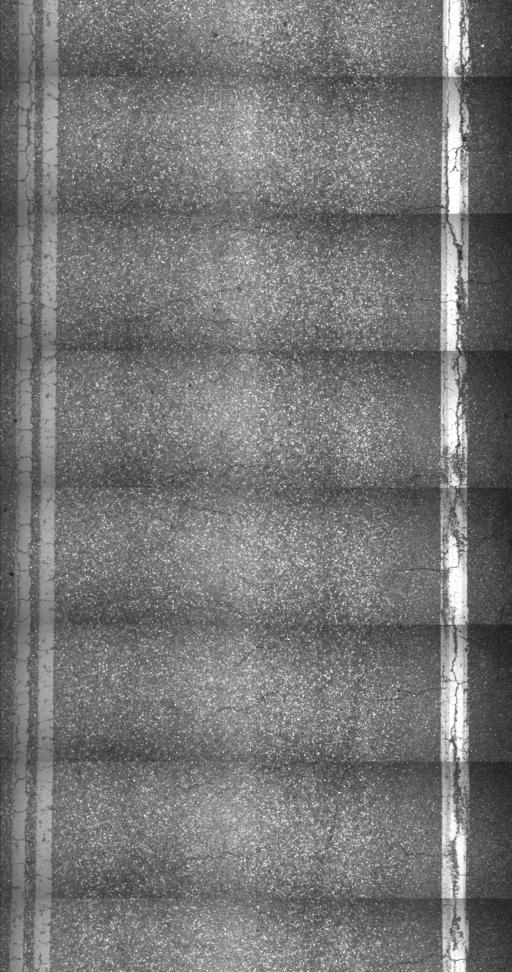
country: US
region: Vermont
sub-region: Franklin County
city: Enosburg Falls
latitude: 44.7939
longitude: -72.8747
